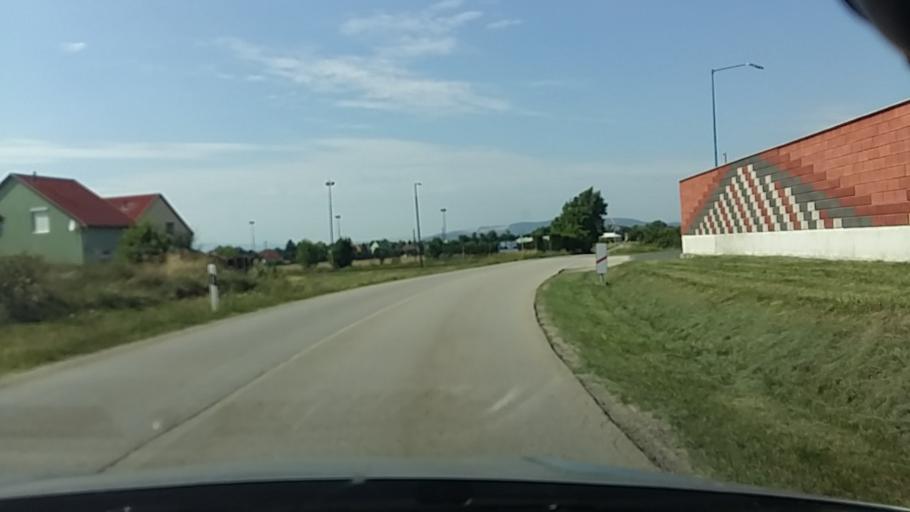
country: HU
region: Pest
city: God
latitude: 47.6939
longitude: 19.1568
